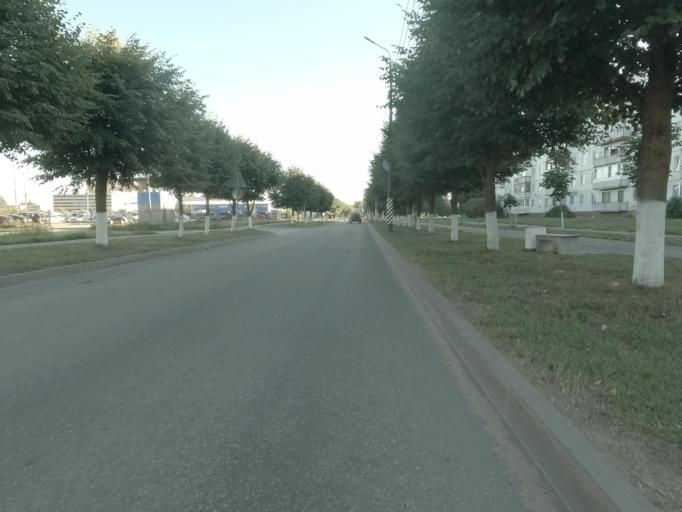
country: RU
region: Leningrad
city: Kirovsk
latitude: 59.8833
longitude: 30.9993
